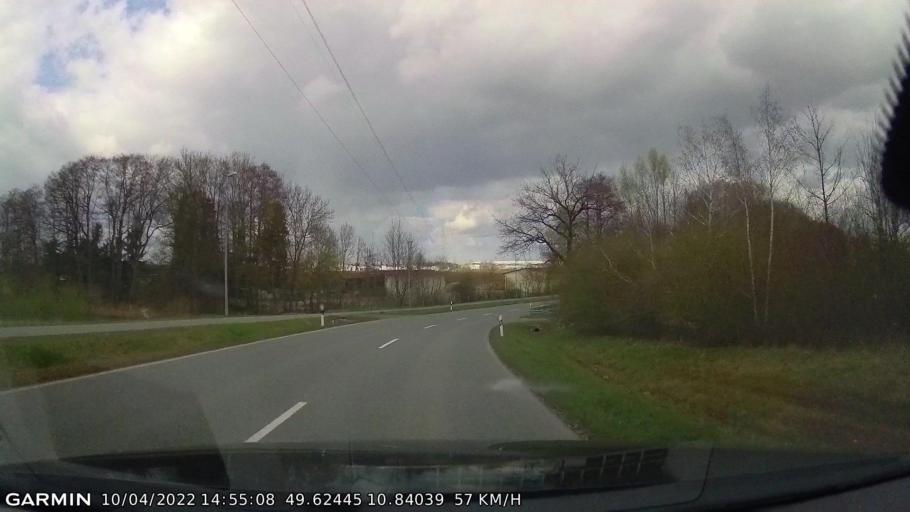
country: DE
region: Bavaria
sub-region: Regierungsbezirk Mittelfranken
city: Weisendorf
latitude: 49.6245
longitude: 10.8405
